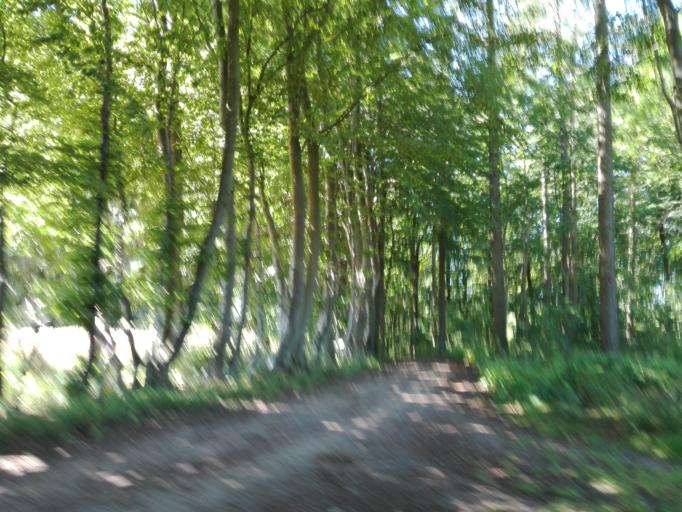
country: DK
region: Central Jutland
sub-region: Odder Kommune
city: Odder
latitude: 55.9658
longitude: 10.1395
